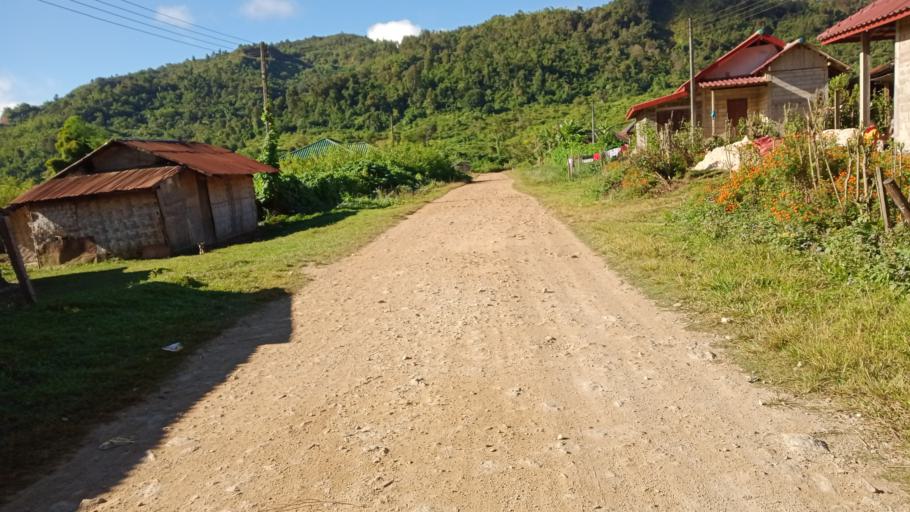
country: LA
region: Xiangkhoang
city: Phonsavan
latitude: 19.1139
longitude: 102.9166
